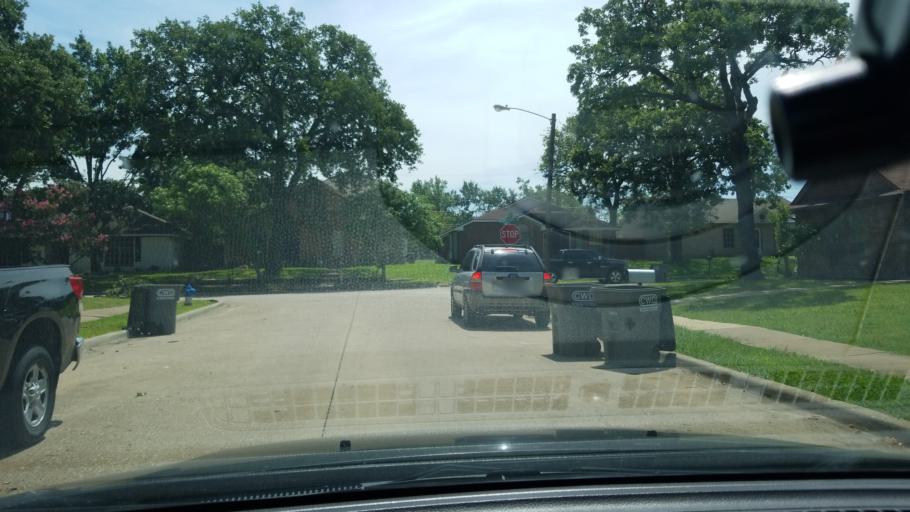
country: US
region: Texas
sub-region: Dallas County
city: Balch Springs
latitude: 32.7397
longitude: -96.6236
